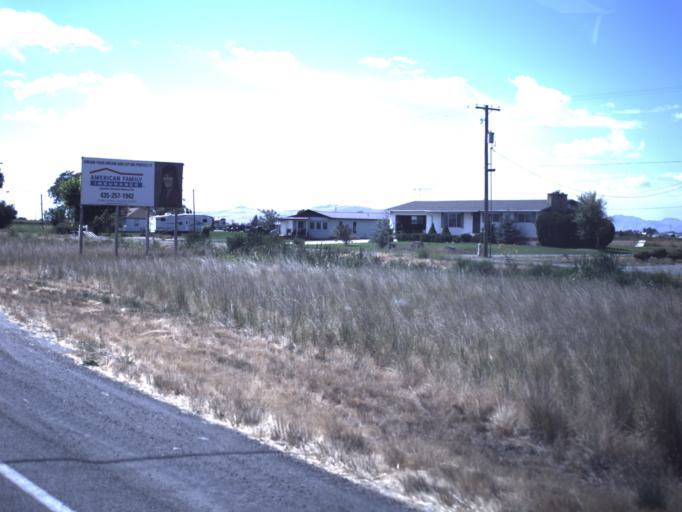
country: US
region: Utah
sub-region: Box Elder County
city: Elwood
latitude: 41.7109
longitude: -112.1422
